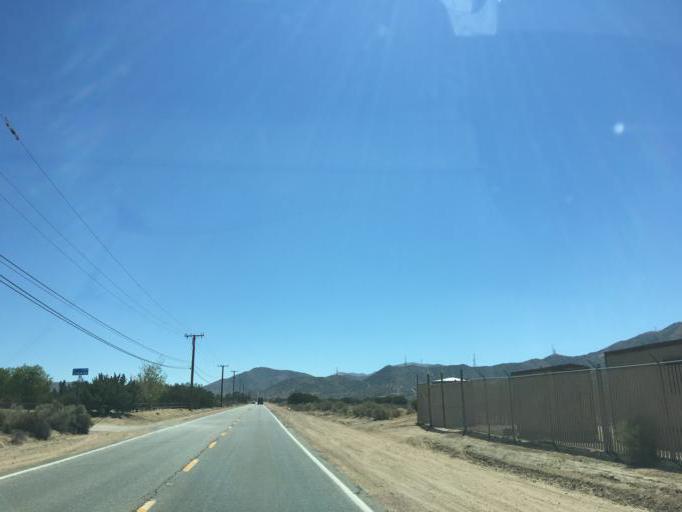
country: US
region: California
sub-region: Los Angeles County
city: Acton
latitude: 34.4809
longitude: -118.1591
